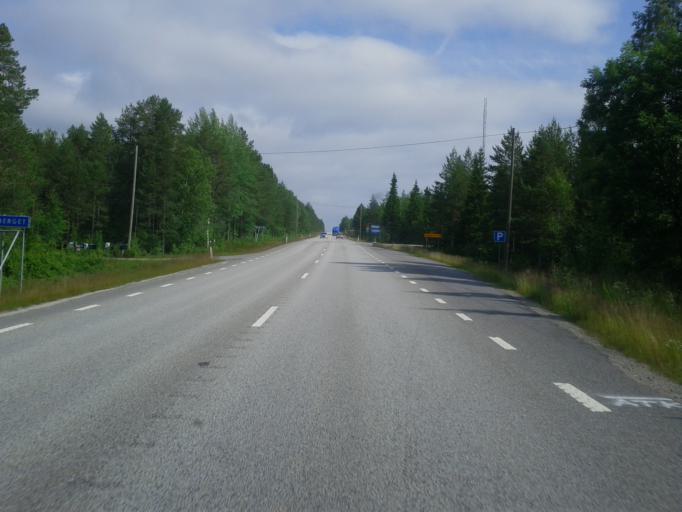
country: SE
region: Vaesterbotten
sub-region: Robertsfors Kommun
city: Robertsfors
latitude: 64.1882
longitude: 20.9966
